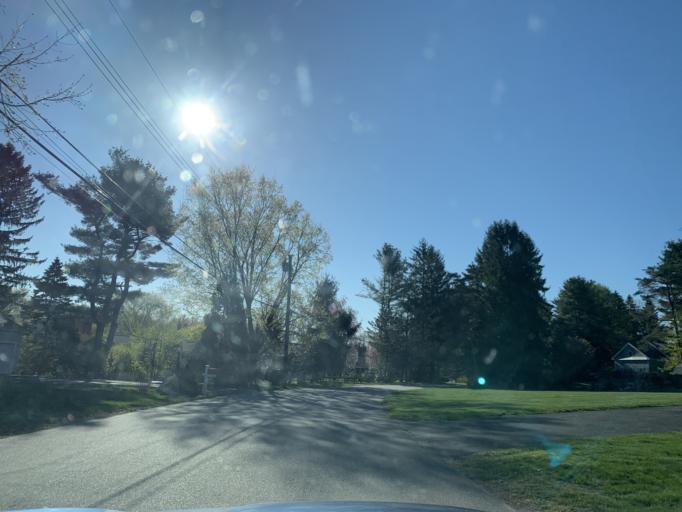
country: US
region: Massachusetts
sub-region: Norfolk County
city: Westwood
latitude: 42.2353
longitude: -71.2148
